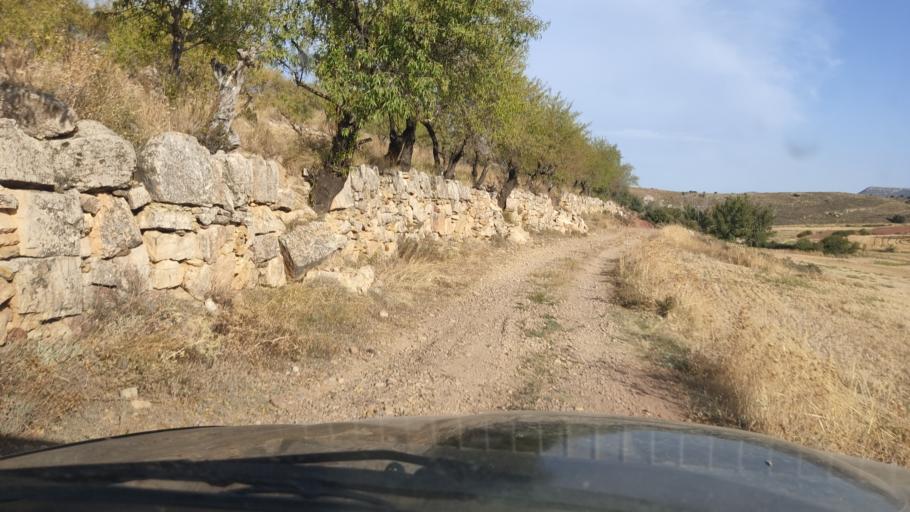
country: ES
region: Aragon
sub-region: Provincia de Teruel
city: Monforte de Moyuela
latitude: 41.0312
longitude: -1.0123
